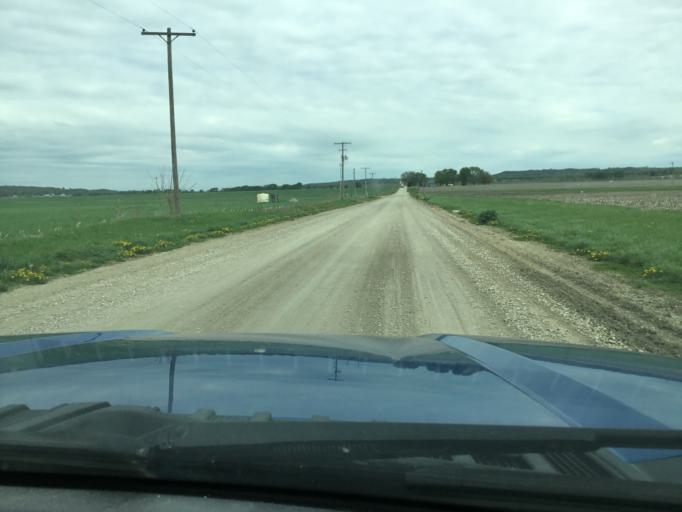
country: US
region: Kansas
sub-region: Douglas County
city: Lawrence
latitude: 39.0132
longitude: -95.2241
